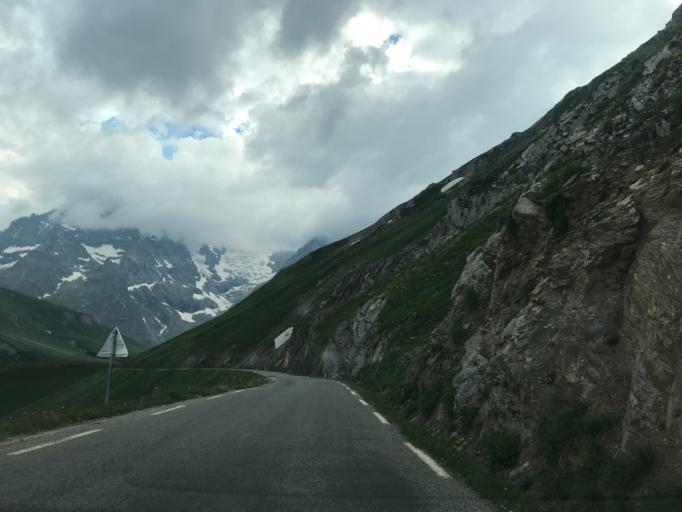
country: FR
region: Provence-Alpes-Cote d'Azur
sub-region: Departement des Hautes-Alpes
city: Le Monetier-les-Bains
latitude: 45.0435
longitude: 6.4012
